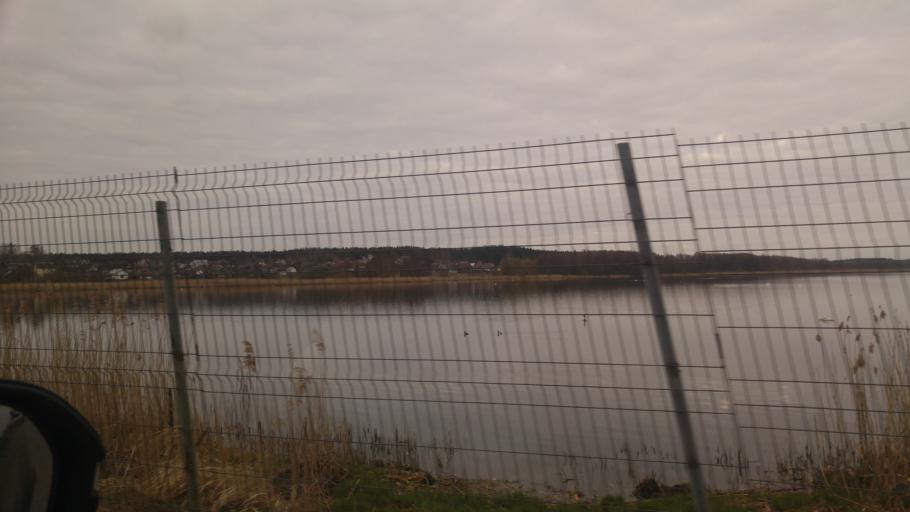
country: BY
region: Minsk
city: Smilavichy
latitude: 53.7180
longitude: 28.1429
